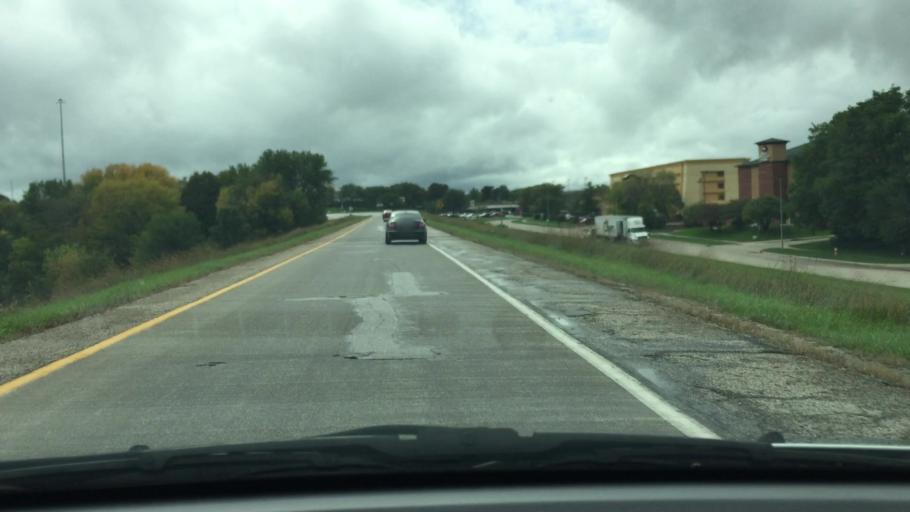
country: US
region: Iowa
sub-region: Polk County
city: Clive
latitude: 41.6043
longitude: -93.7780
